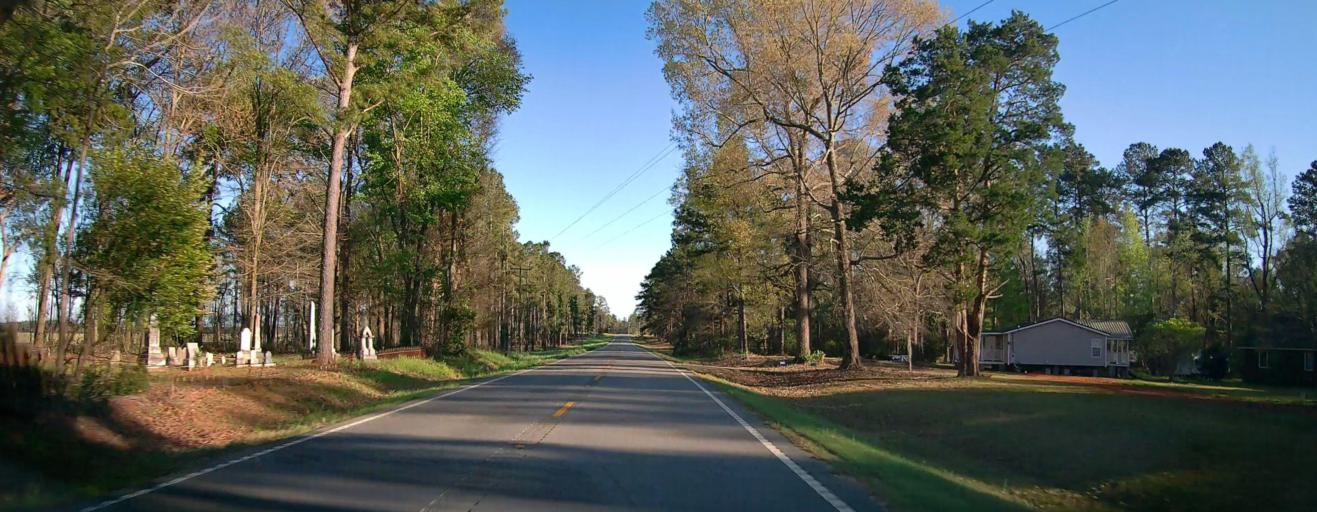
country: US
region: Georgia
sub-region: Pulaski County
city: Hawkinsville
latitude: 32.2153
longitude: -83.3841
